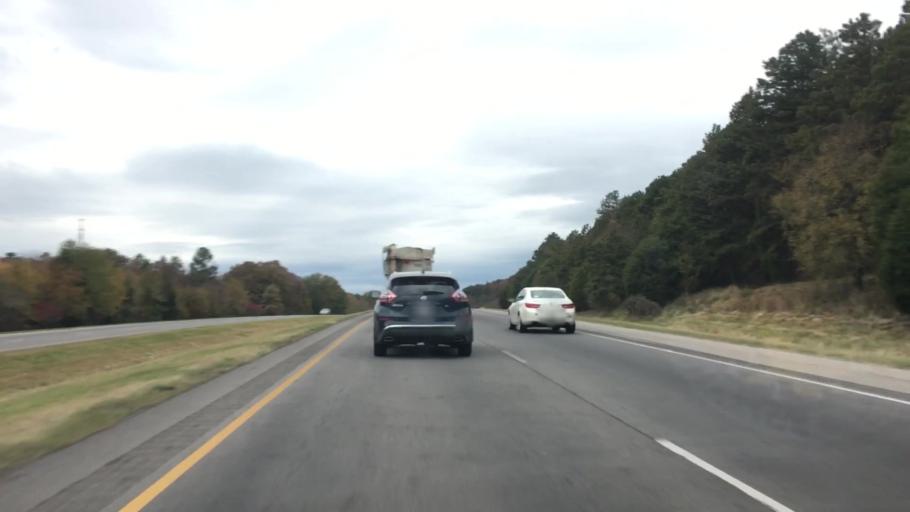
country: US
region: Arkansas
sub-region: Johnson County
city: Coal Hill
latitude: 35.5005
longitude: -93.7217
